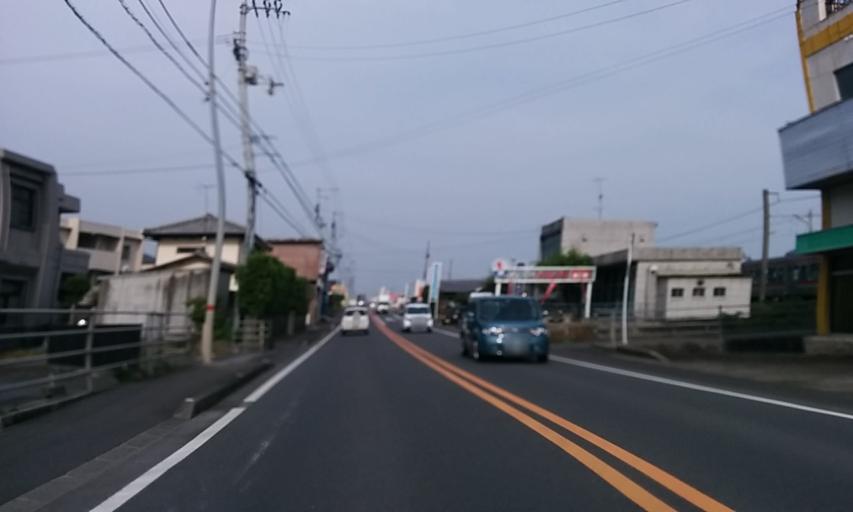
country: JP
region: Ehime
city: Kawanoecho
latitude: 33.9680
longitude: 133.5102
